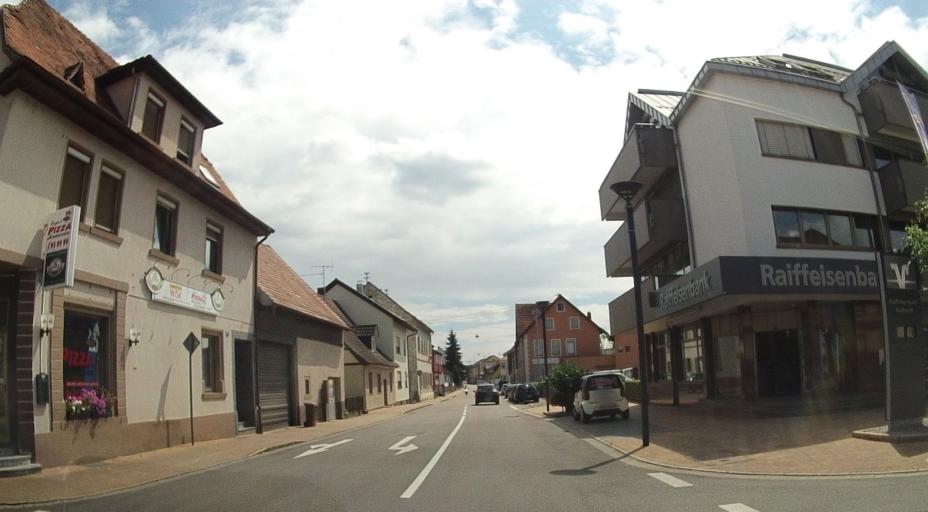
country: DE
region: Baden-Wuerttemberg
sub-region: Karlsruhe Region
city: Durmersheim
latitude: 48.9295
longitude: 8.2671
